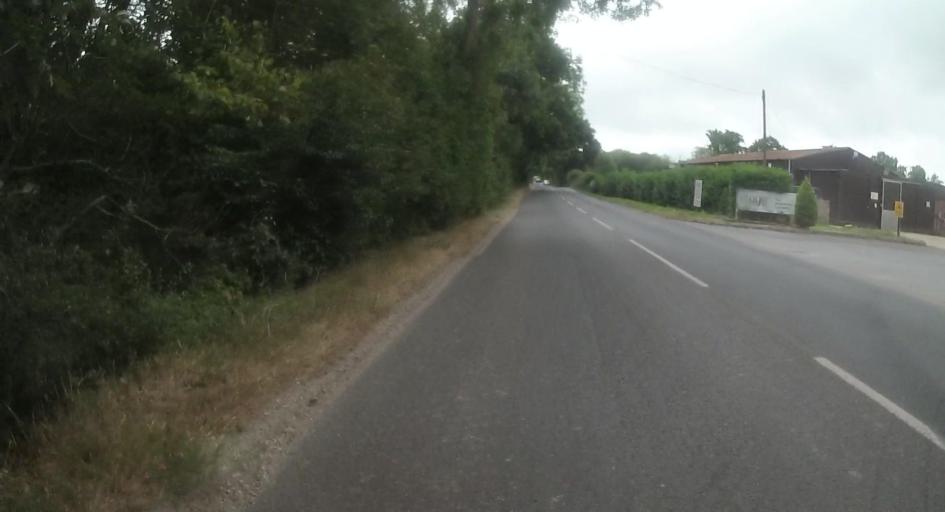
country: GB
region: England
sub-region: Dorset
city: Bovington Camp
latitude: 50.7169
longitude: -2.2873
